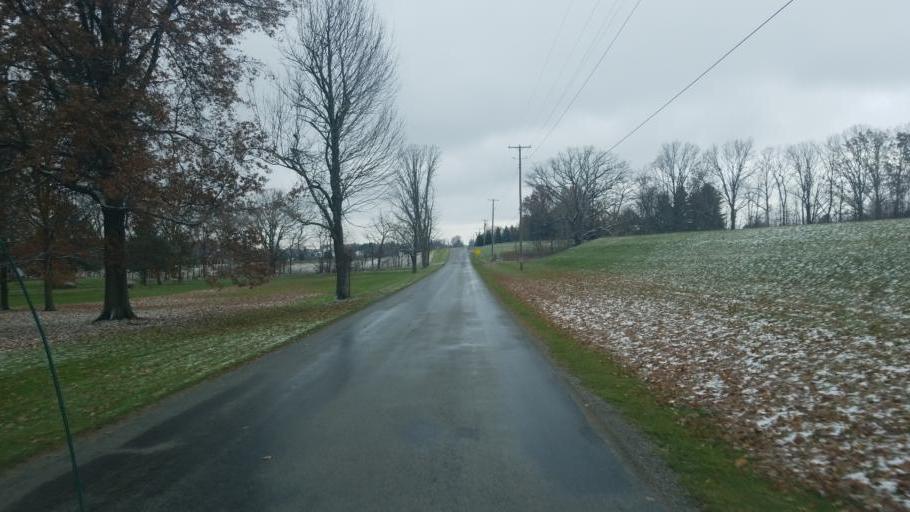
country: US
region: Ohio
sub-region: Richland County
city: Shelby
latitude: 40.8636
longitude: -82.5956
